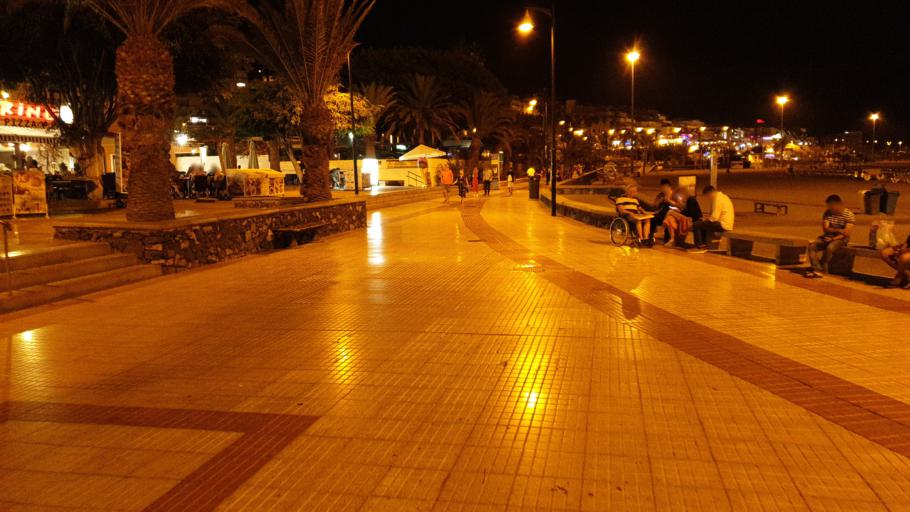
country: ES
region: Canary Islands
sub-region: Provincia de Santa Cruz de Tenerife
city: Playa de las Americas
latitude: 28.0534
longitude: -16.7260
